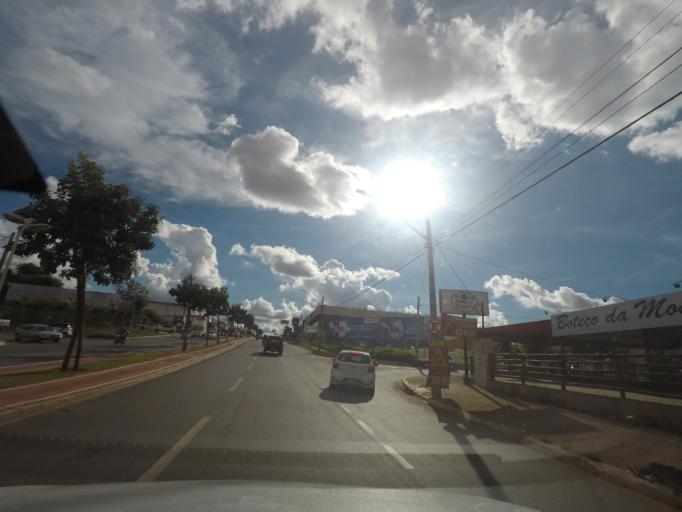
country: BR
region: Goias
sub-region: Goiania
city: Goiania
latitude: -16.7180
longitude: -49.2954
